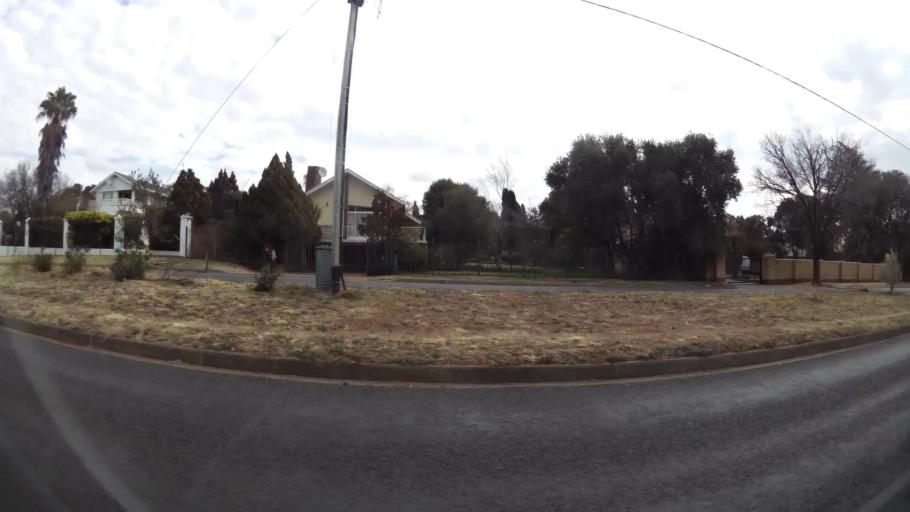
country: ZA
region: Orange Free State
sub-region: Mangaung Metropolitan Municipality
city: Bloemfontein
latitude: -29.0979
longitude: 26.2125
